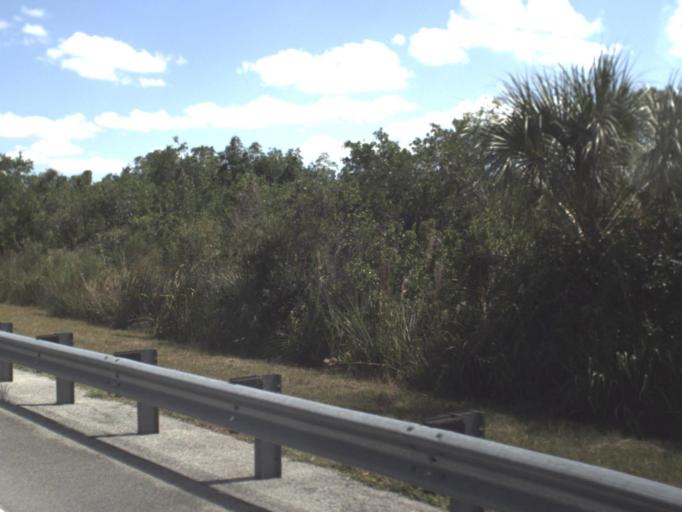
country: US
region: Florida
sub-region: Collier County
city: Marco
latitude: 25.9877
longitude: -81.5792
